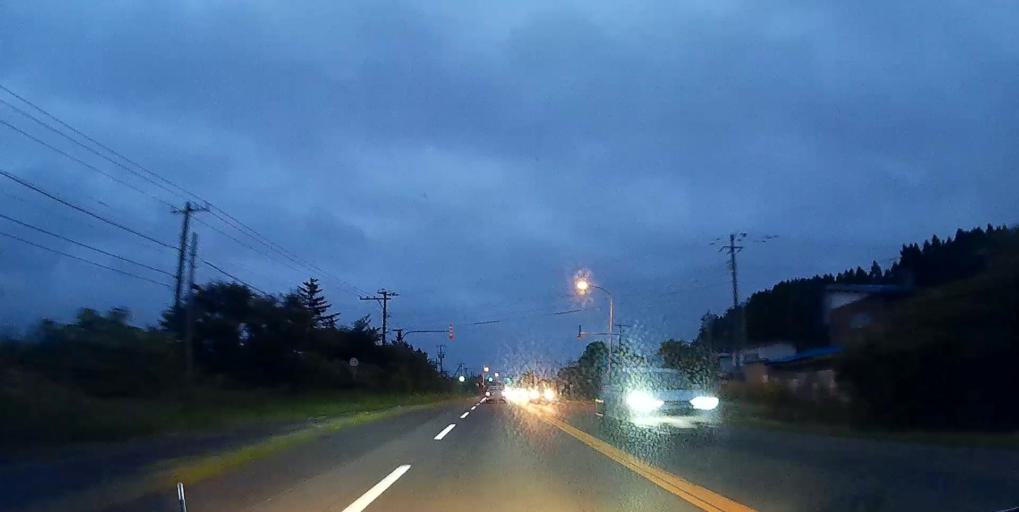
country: JP
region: Hokkaido
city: Nanae
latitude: 42.2224
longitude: 140.3677
